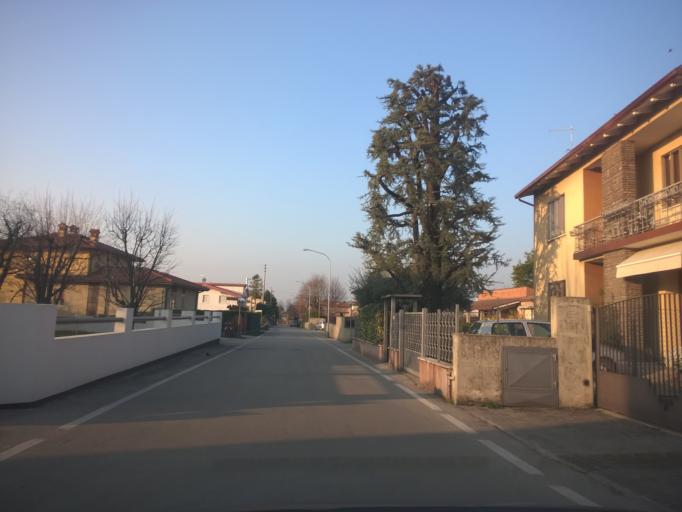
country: IT
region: Veneto
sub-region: Provincia di Vicenza
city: Zane
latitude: 45.7226
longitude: 11.4543
